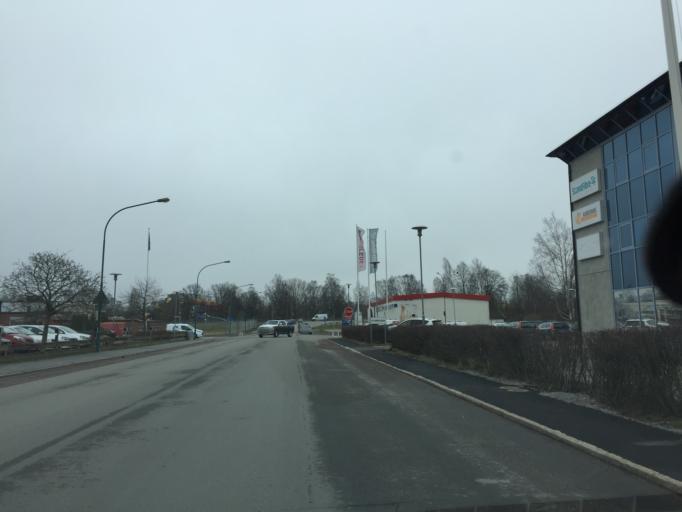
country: SE
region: OErebro
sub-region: Orebro Kommun
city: Orebro
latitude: 59.2607
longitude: 15.1868
